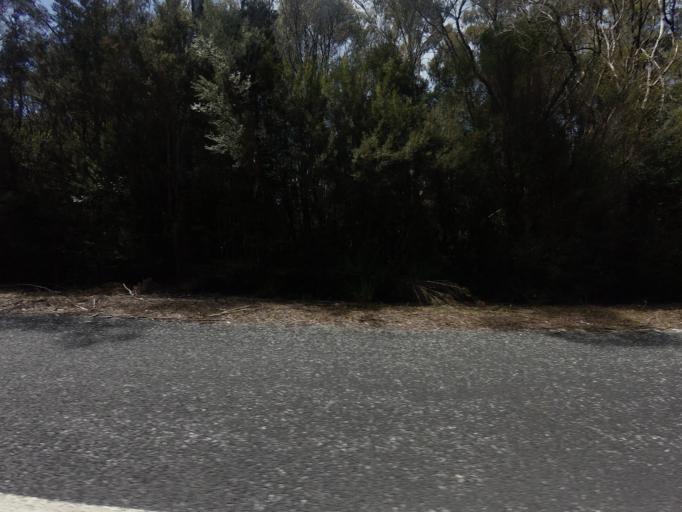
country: AU
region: Tasmania
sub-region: West Coast
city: Queenstown
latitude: -42.8027
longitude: 146.0960
